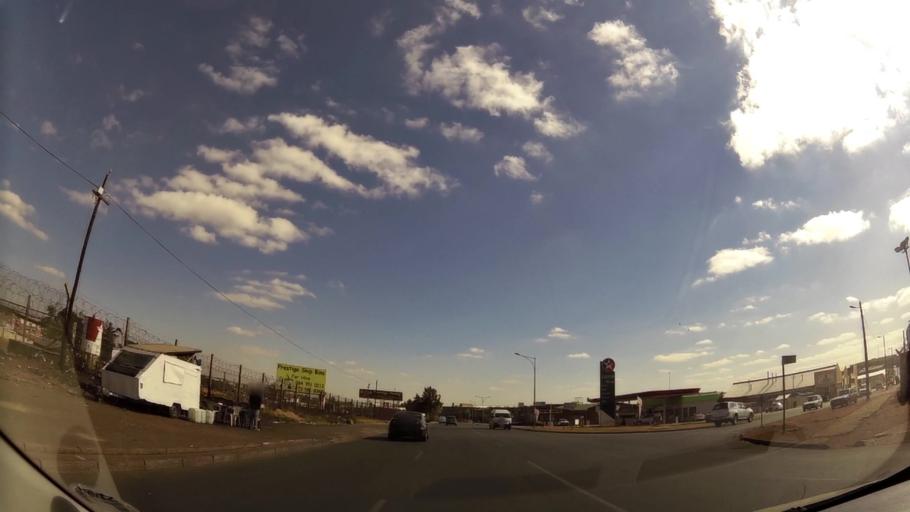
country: ZA
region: Gauteng
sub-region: West Rand District Municipality
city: Krugersdorp
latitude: -26.1189
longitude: 27.8108
